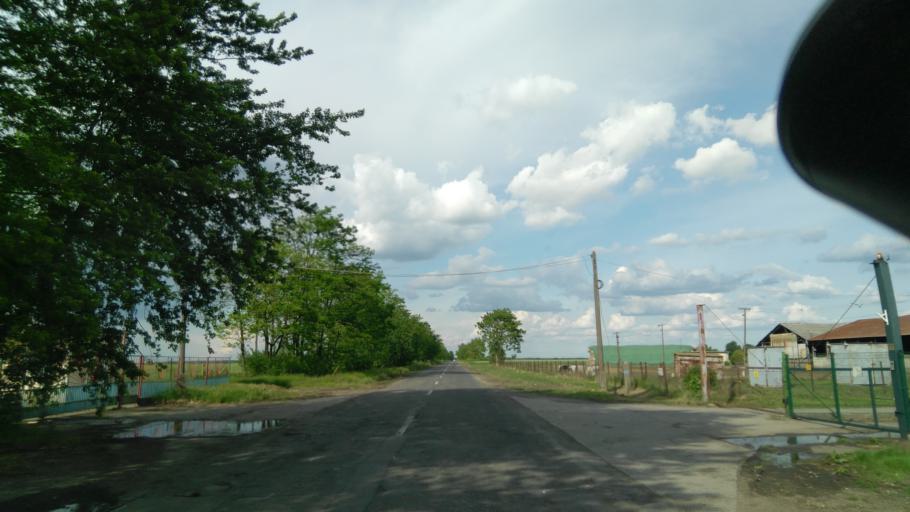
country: HU
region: Bekes
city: Battonya
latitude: 46.2987
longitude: 21.0480
